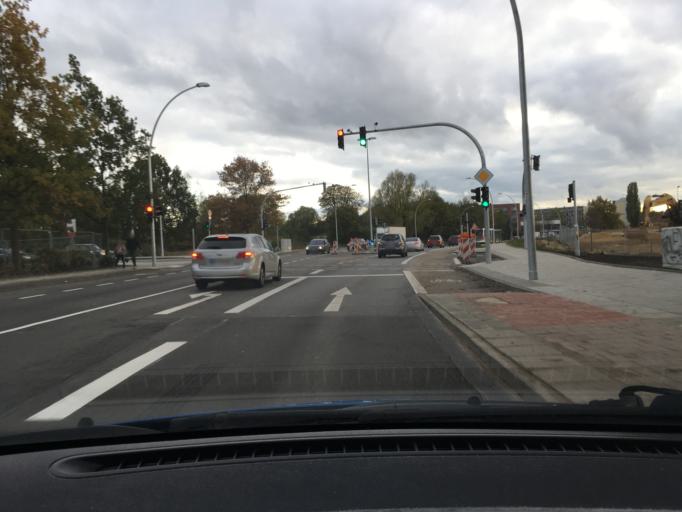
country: DE
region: Hamburg
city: Kleiner Grasbrook
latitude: 53.5030
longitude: 10.0039
